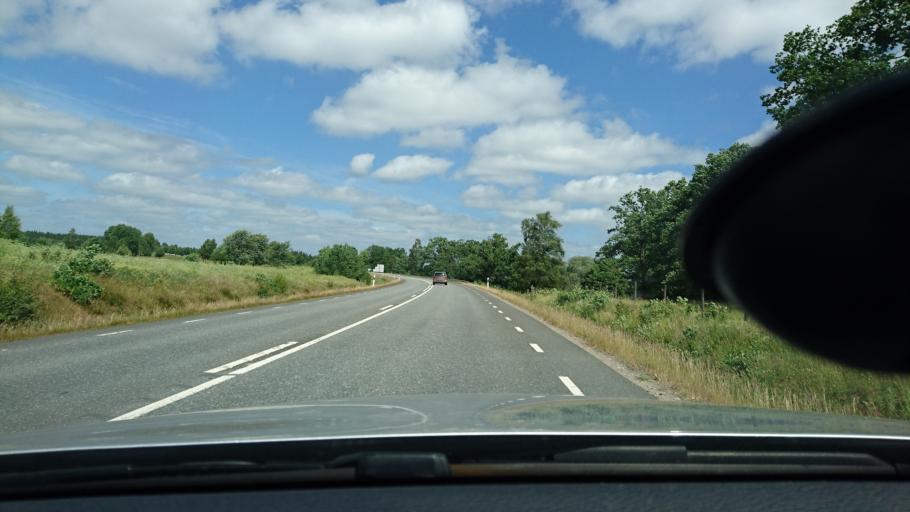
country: SE
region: Kronoberg
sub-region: Alvesta Kommun
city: Moheda
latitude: 56.9579
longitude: 14.5716
